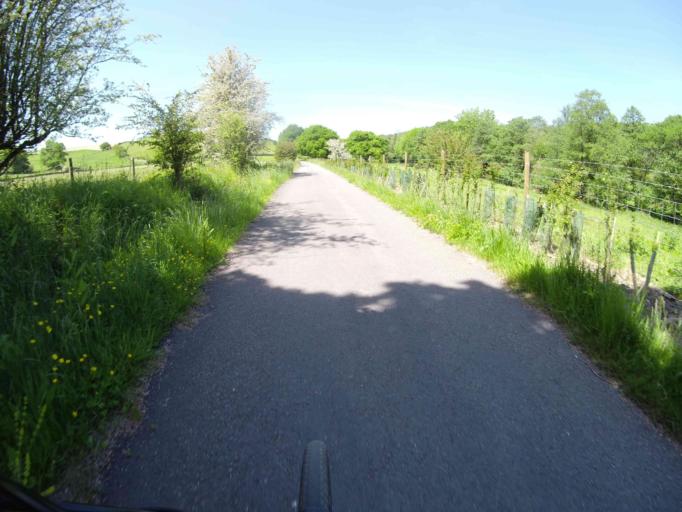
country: GB
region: England
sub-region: Devon
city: Bovey Tracey
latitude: 50.6431
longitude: -3.7386
